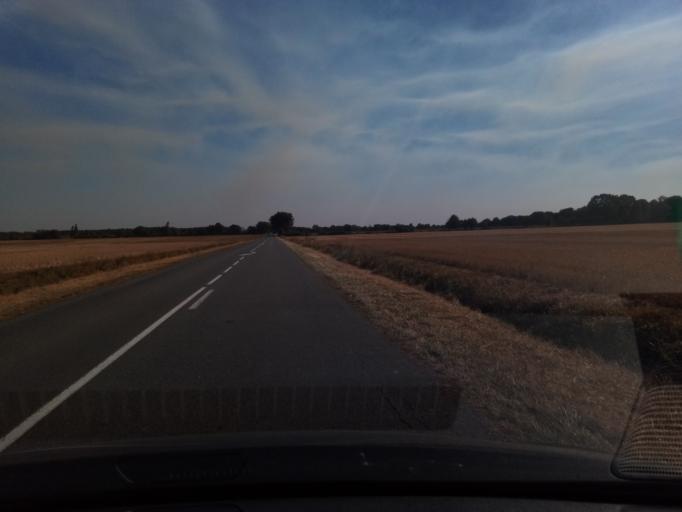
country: FR
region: Poitou-Charentes
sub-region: Departement de la Vienne
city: Montmorillon
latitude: 46.4938
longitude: 0.7830
